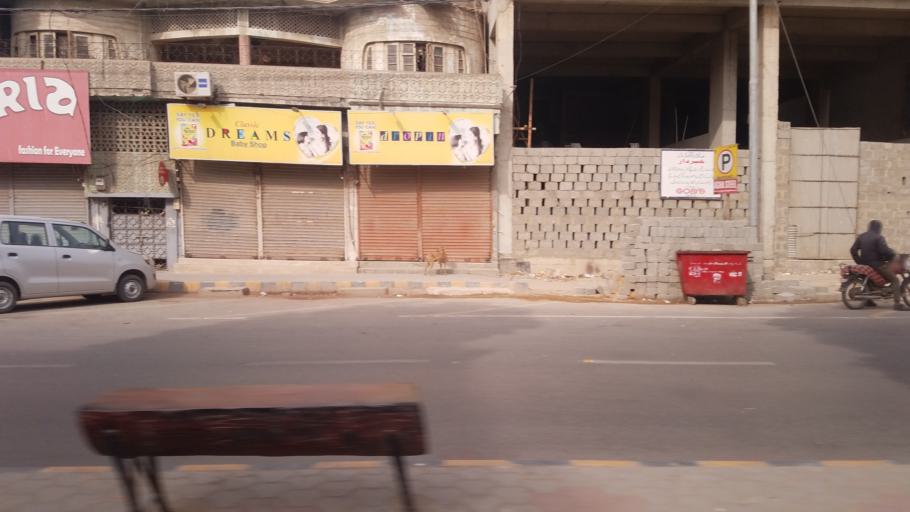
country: PK
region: Sindh
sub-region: Karachi District
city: Karachi
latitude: 24.8699
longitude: 67.0586
